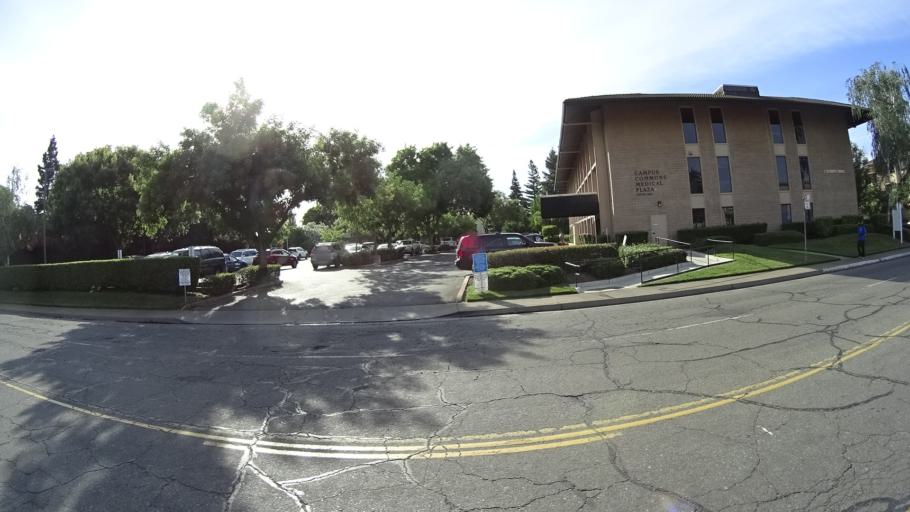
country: US
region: California
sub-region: Sacramento County
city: Arden-Arcade
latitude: 38.5735
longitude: -121.4122
